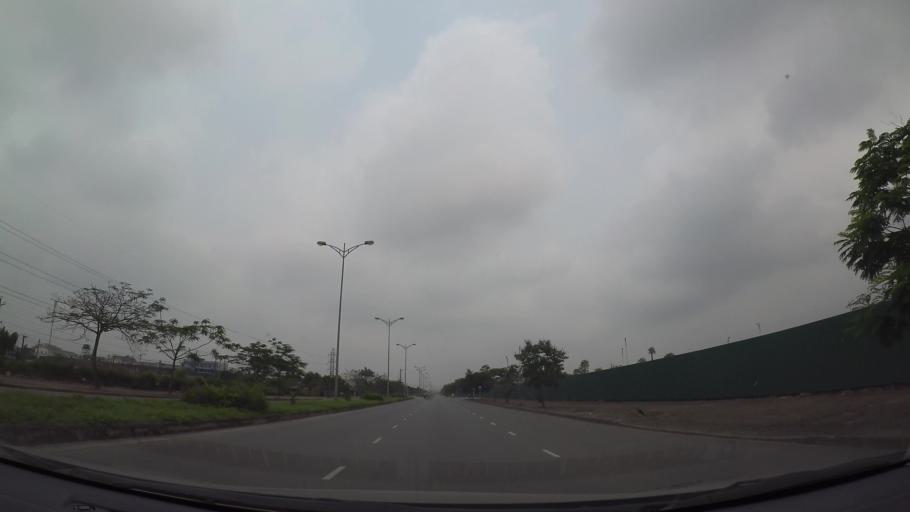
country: VN
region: Ha Noi
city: Trau Quy
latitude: 21.0355
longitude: 105.9235
